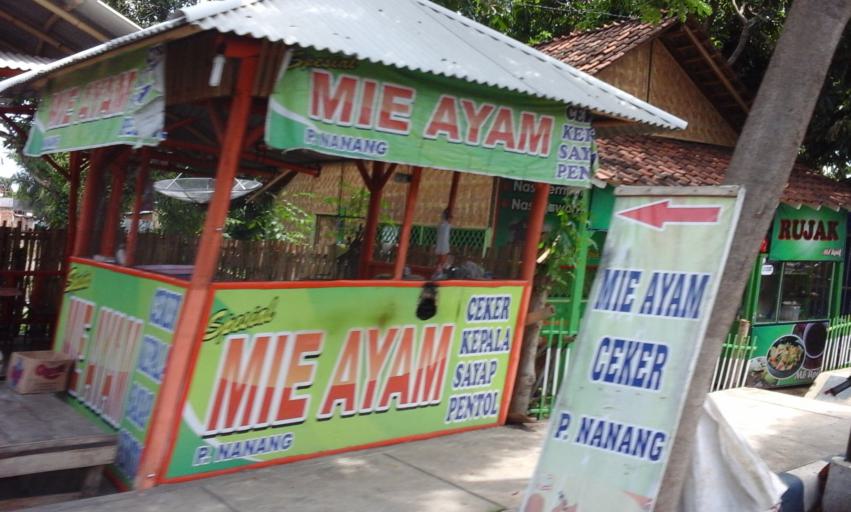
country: ID
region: East Java
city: Cungking
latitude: -8.2192
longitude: 114.3532
